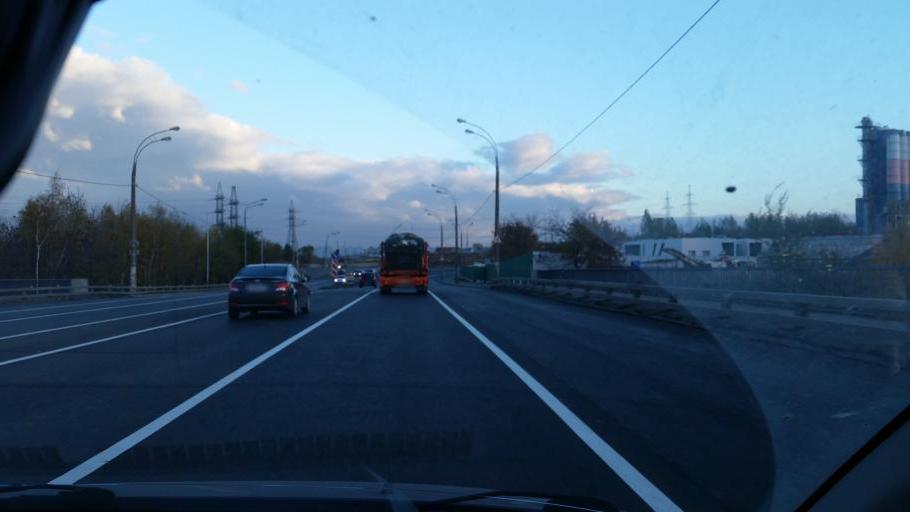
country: RU
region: Moskovskaya
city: Biryulevo Zapadnoye
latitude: 55.6039
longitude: 37.6339
